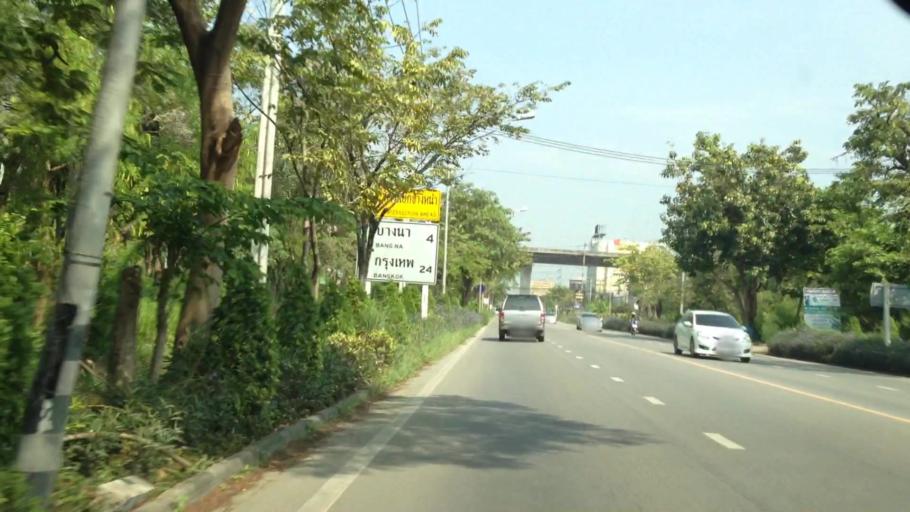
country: TH
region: Bangkok
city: Bang Na
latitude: 13.6629
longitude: 100.6450
